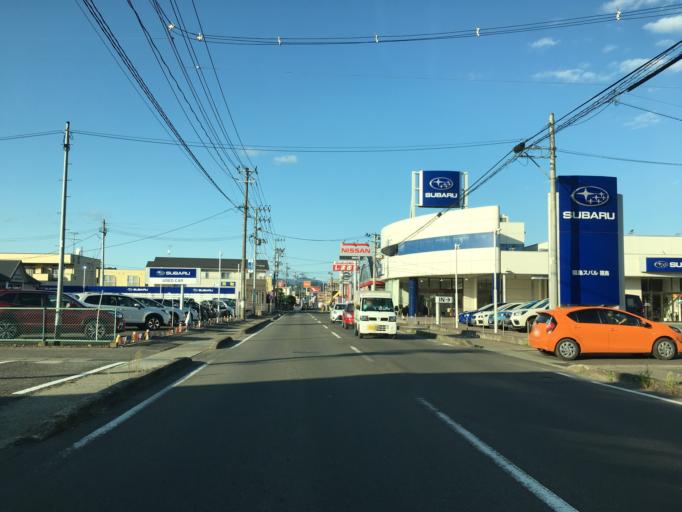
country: JP
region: Fukushima
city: Fukushima-shi
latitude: 37.7316
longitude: 140.4598
